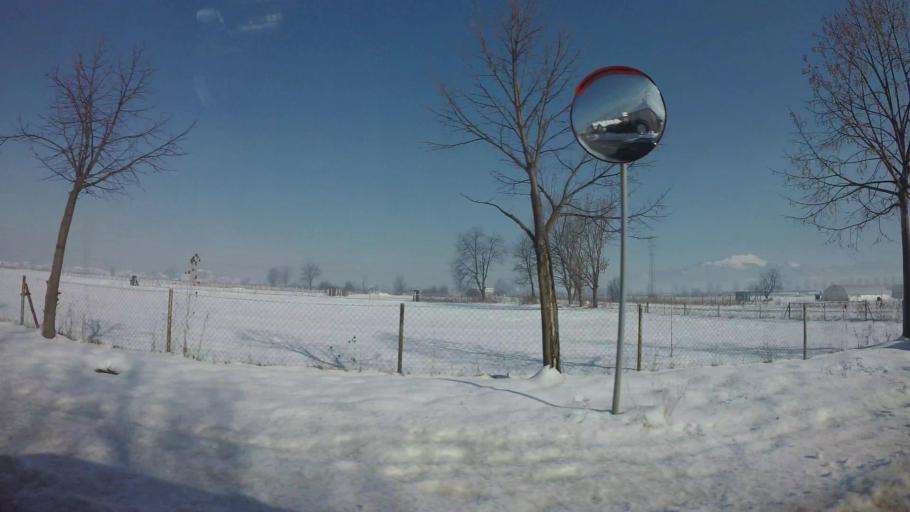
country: BA
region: Federation of Bosnia and Herzegovina
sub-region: Kanton Sarajevo
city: Sarajevo
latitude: 43.8032
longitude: 18.3058
